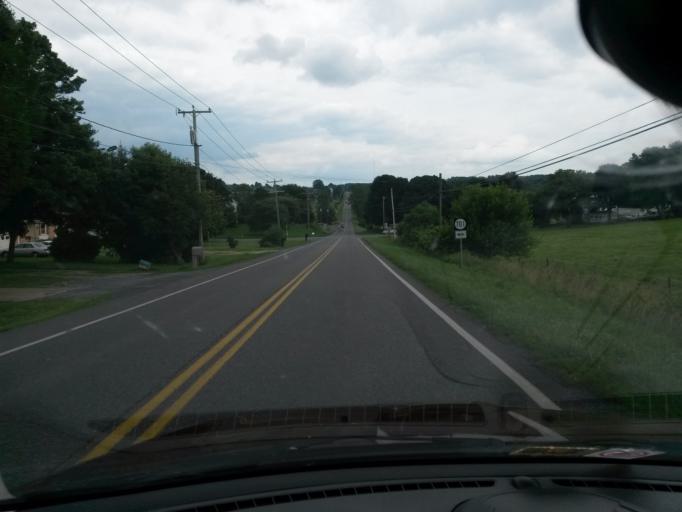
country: US
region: Virginia
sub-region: Rockingham County
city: Dayton
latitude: 38.4540
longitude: -78.9329
